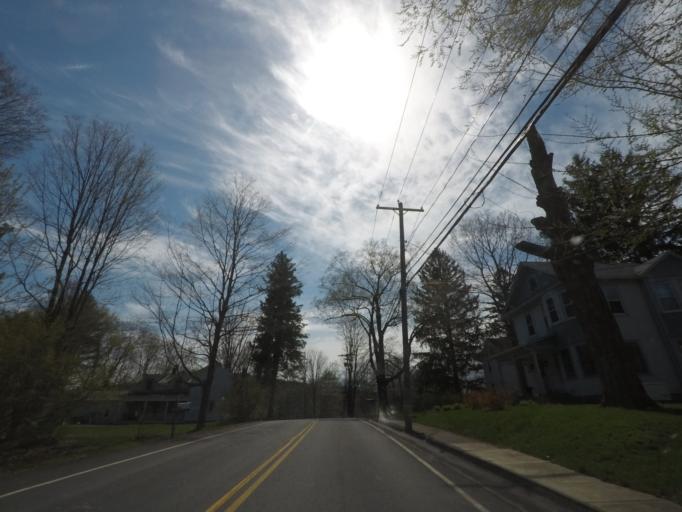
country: US
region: New York
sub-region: Columbia County
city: Chatham
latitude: 42.4101
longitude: -73.5252
